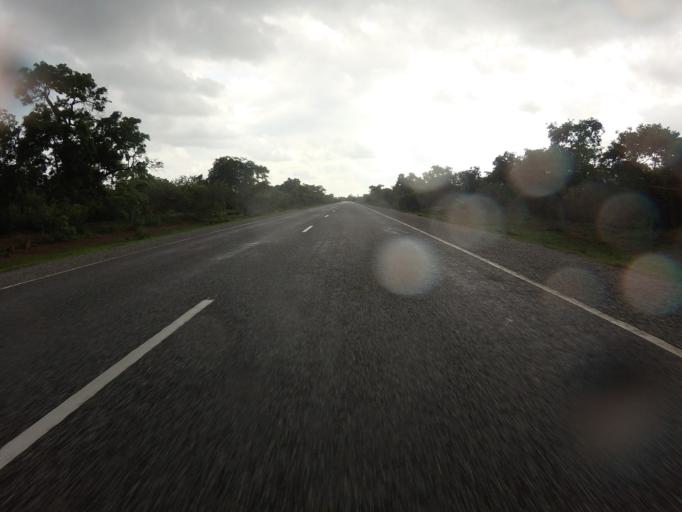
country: GH
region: Northern
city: Tamale
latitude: 9.1217
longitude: -1.6412
